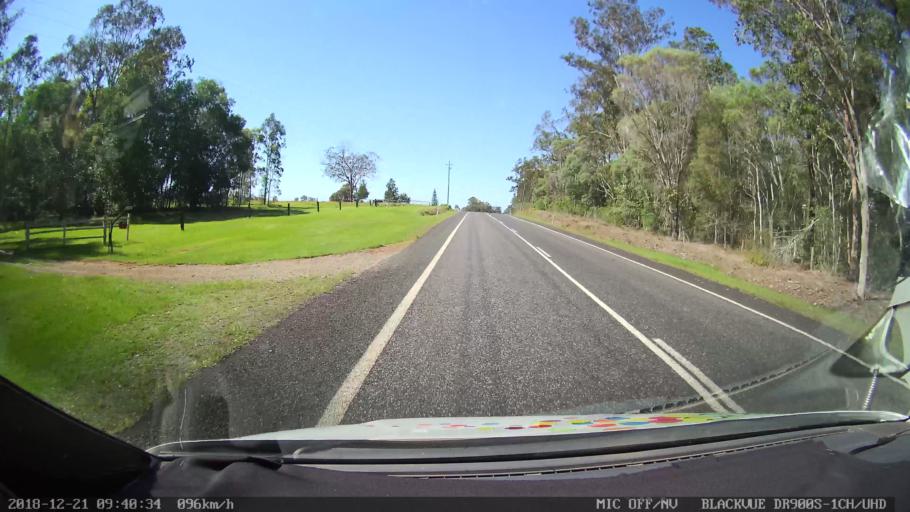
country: AU
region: New South Wales
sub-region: Clarence Valley
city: Grafton
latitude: -29.5744
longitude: 152.9631
